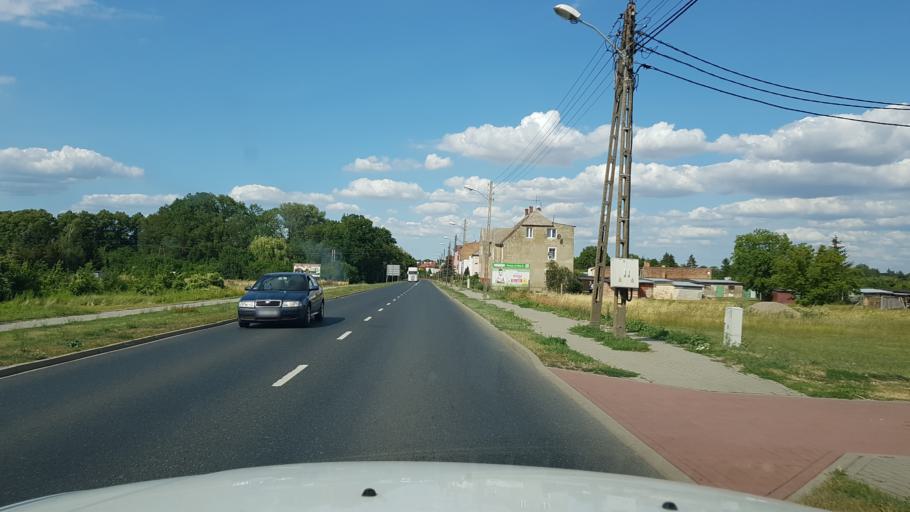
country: PL
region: West Pomeranian Voivodeship
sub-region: Powiat pyrzycki
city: Pyrzyce
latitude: 53.1316
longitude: 14.8910
